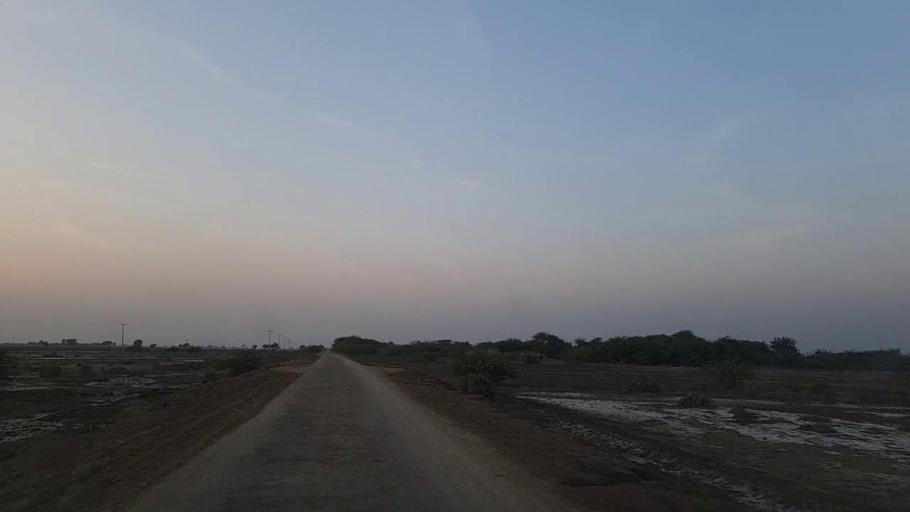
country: PK
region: Sindh
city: Naukot
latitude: 24.9758
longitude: 69.4313
